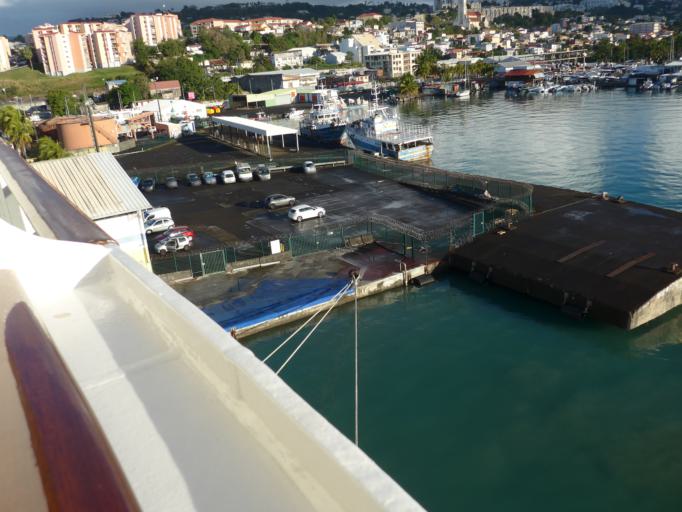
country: MQ
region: Martinique
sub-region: Martinique
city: Fort-de-France
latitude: 14.6020
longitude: -61.0593
